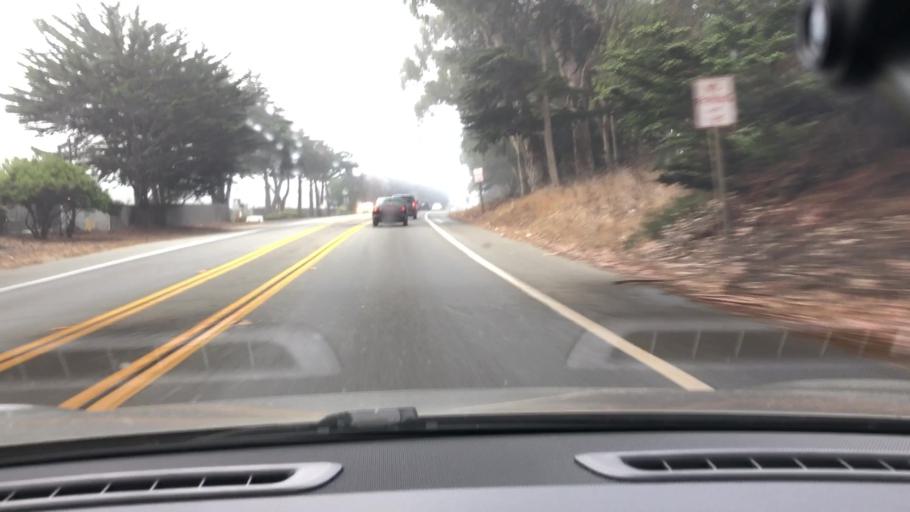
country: US
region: California
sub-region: Monterey County
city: Elkhorn
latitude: 36.8073
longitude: -121.7840
